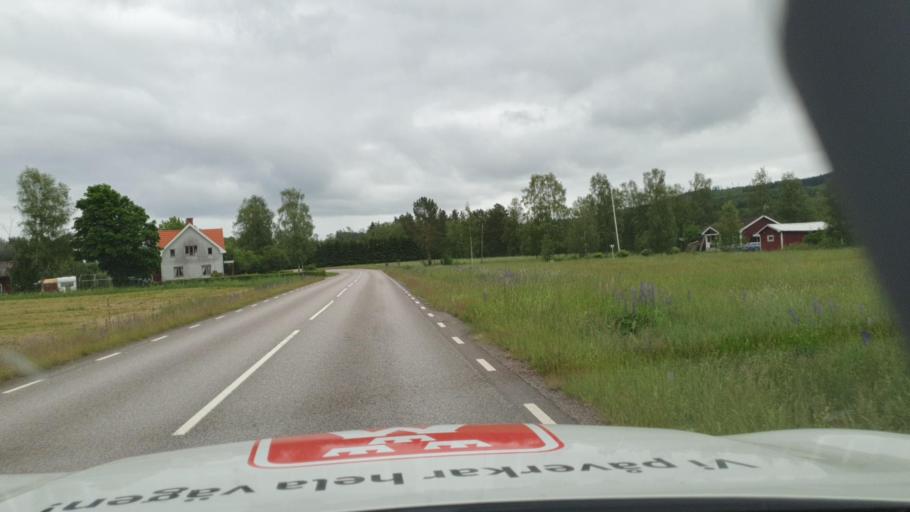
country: SE
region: Vaermland
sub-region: Sunne Kommun
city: Sunne
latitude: 59.7959
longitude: 13.0689
